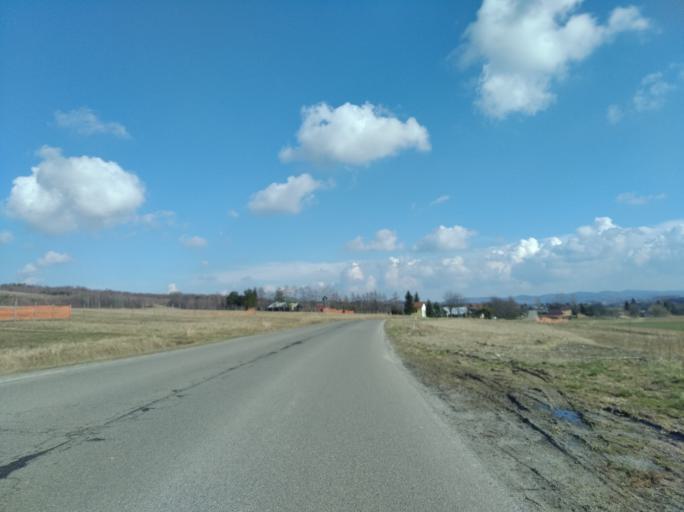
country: PL
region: Subcarpathian Voivodeship
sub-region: Powiat strzyzowski
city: Frysztak
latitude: 49.8499
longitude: 21.5292
